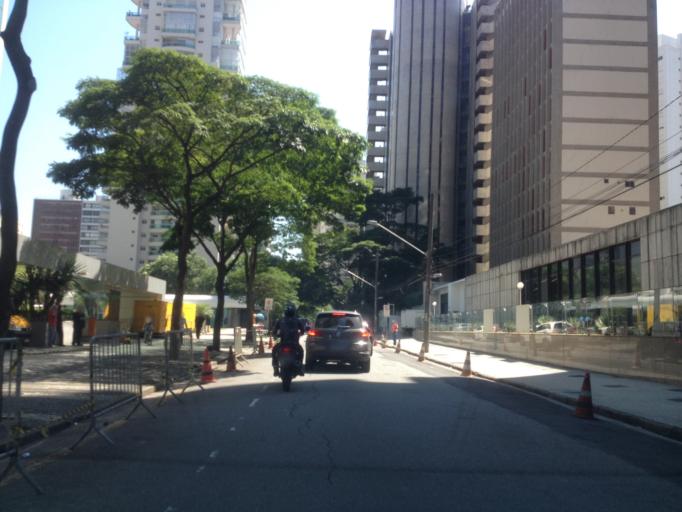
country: BR
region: Sao Paulo
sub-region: Sao Paulo
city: Sao Paulo
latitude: -23.5598
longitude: -46.6578
